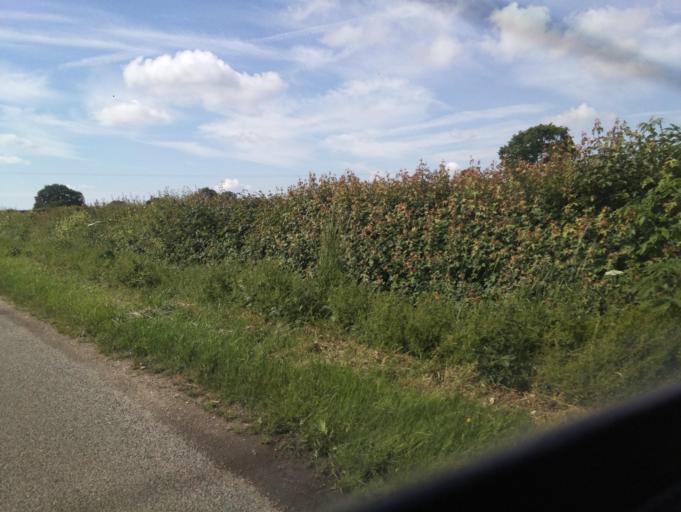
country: GB
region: England
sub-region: Lincolnshire
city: Skellingthorpe
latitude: 53.1405
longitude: -0.6333
